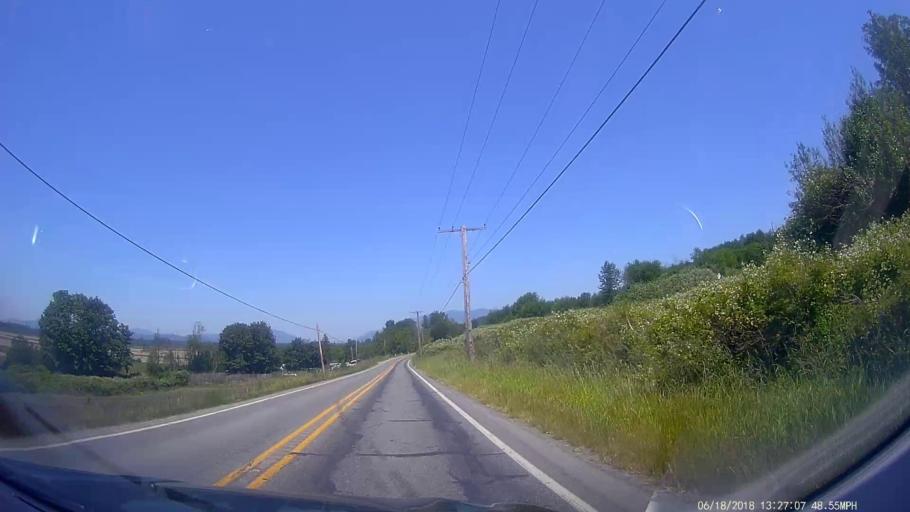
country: US
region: Washington
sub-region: Skagit County
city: Clear Lake
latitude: 48.4380
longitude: -122.2637
